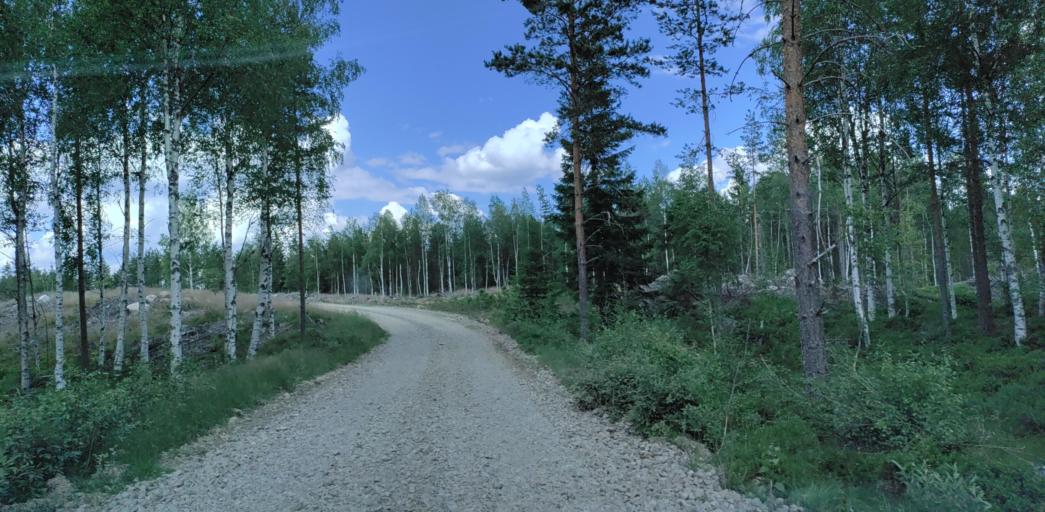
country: SE
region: Vaermland
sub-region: Hagfors Kommun
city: Ekshaerad
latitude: 60.0760
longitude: 13.3459
